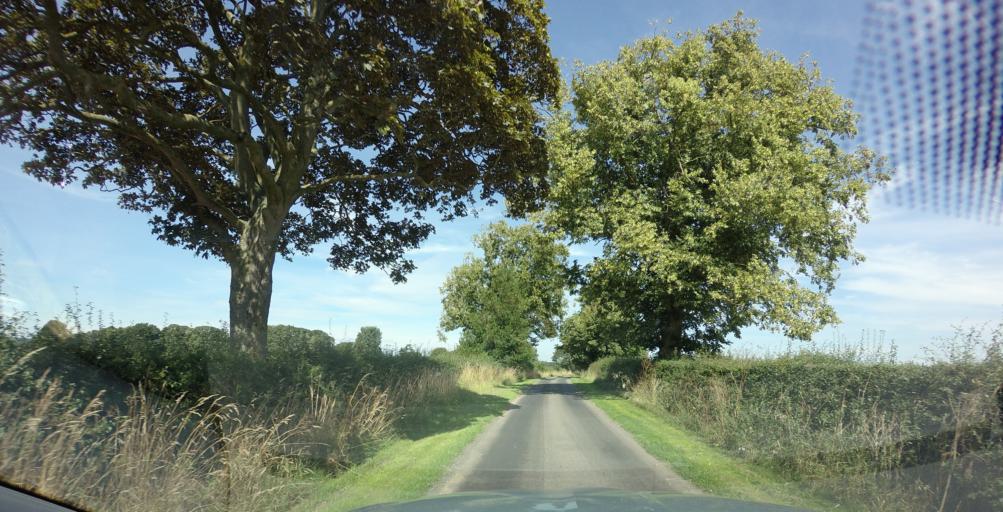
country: GB
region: England
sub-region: North Yorkshire
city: Ripon
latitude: 54.1148
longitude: -1.4819
